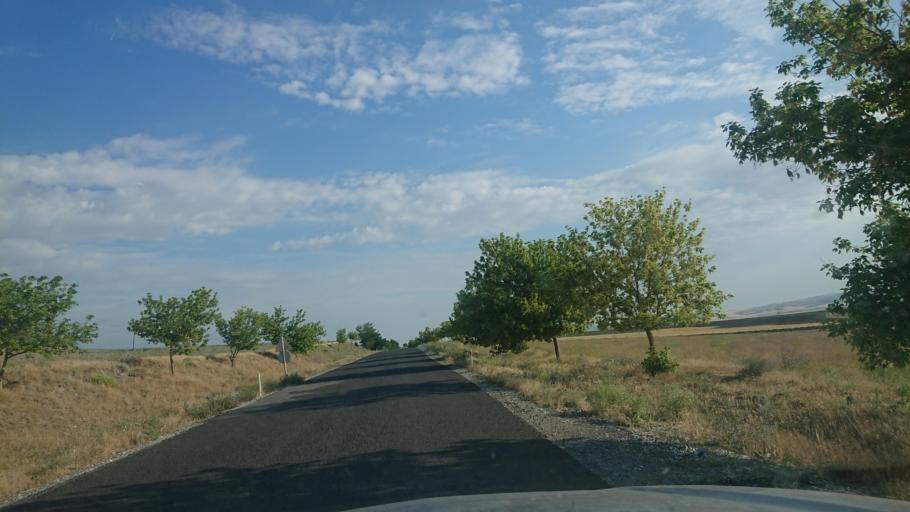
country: TR
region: Aksaray
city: Ortakoy
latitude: 38.8006
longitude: 34.0635
